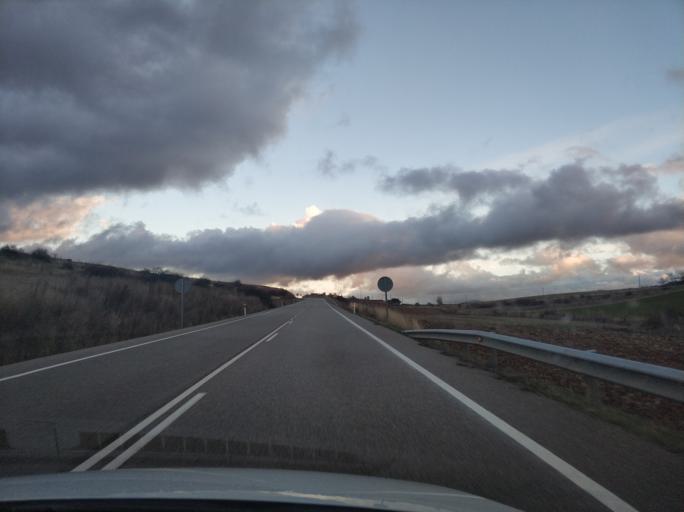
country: ES
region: Castille and Leon
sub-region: Provincia de Segovia
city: Ayllon
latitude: 41.4156
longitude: -3.4036
